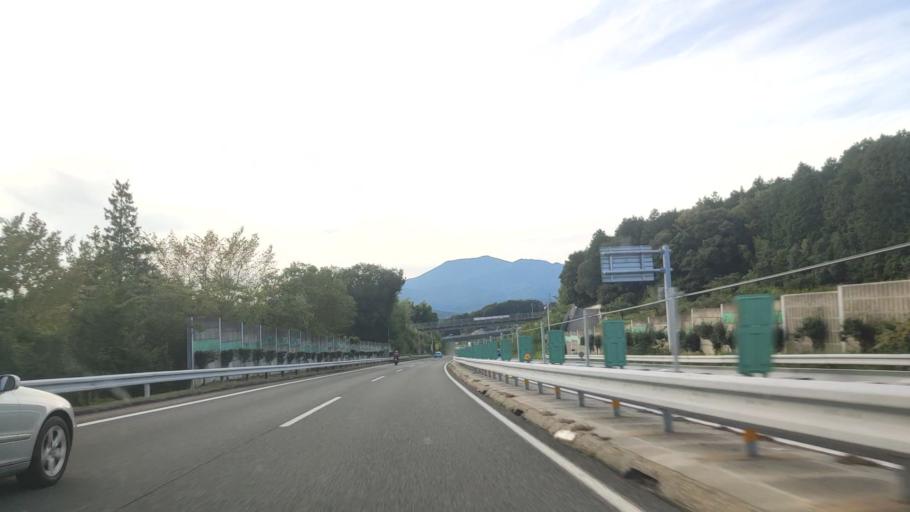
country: JP
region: Gifu
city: Nakatsugawa
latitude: 35.4558
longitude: 137.4209
